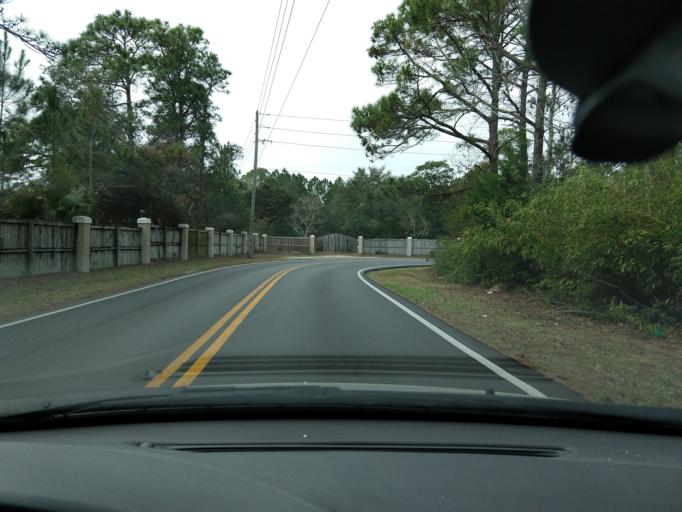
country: US
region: Florida
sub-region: Walton County
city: Miramar Beach
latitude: 30.4052
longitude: -86.3121
